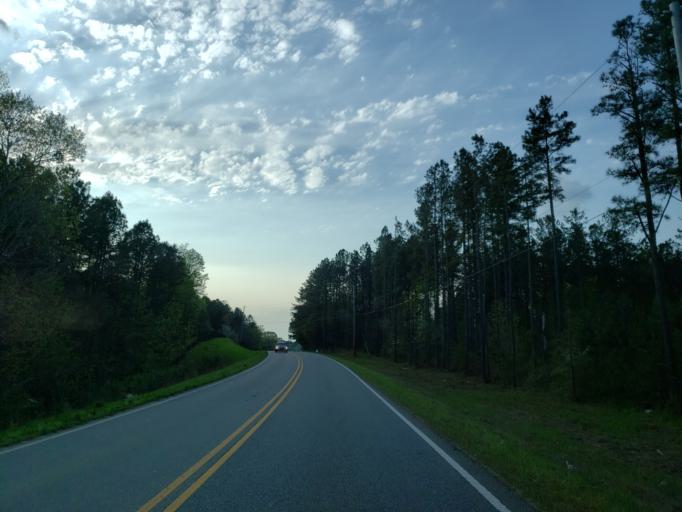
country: US
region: Georgia
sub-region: Cherokee County
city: Ball Ground
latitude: 34.2843
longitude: -84.3805
